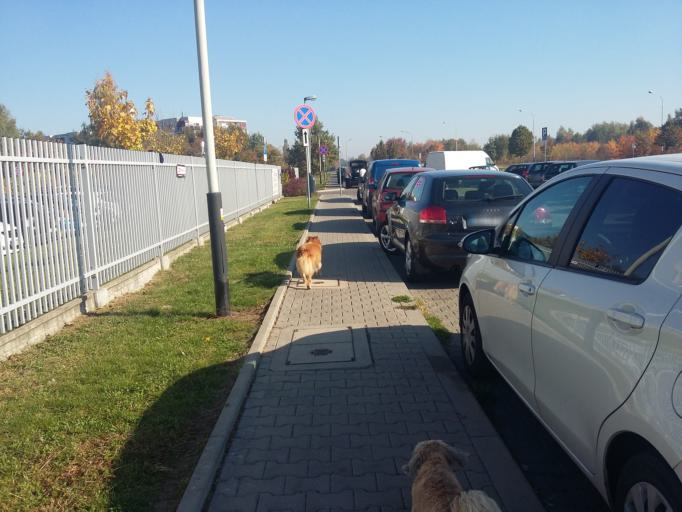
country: PL
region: Lodz Voivodeship
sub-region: Powiat pabianicki
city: Ksawerow
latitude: 51.7341
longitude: 19.4038
